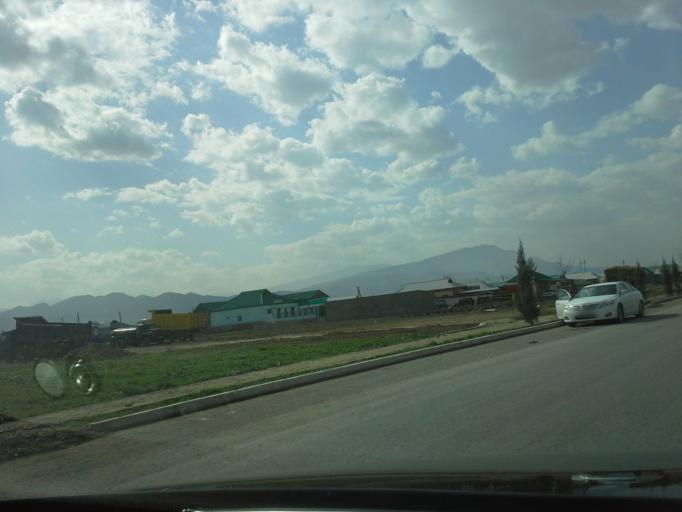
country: TM
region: Ahal
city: Abadan
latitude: 37.9821
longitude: 58.2667
